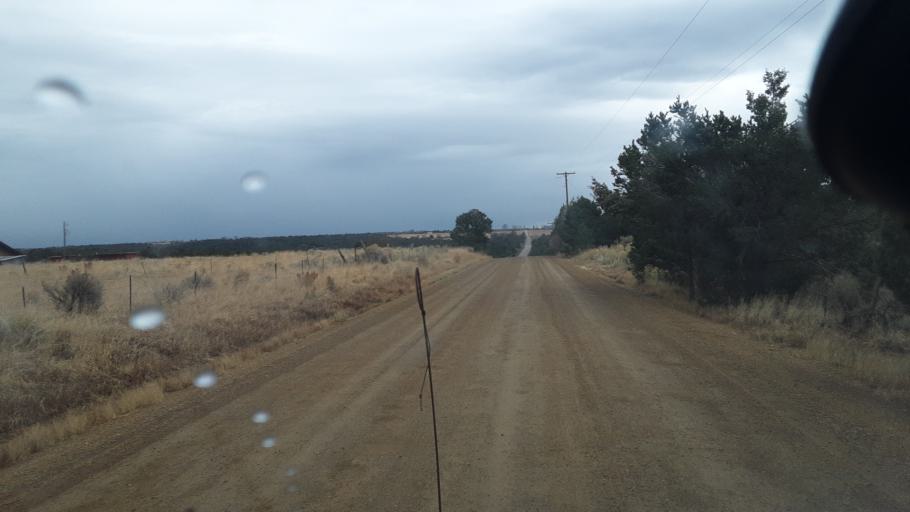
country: US
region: Colorado
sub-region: Montezuma County
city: Mancos
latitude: 37.1985
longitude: -108.1289
